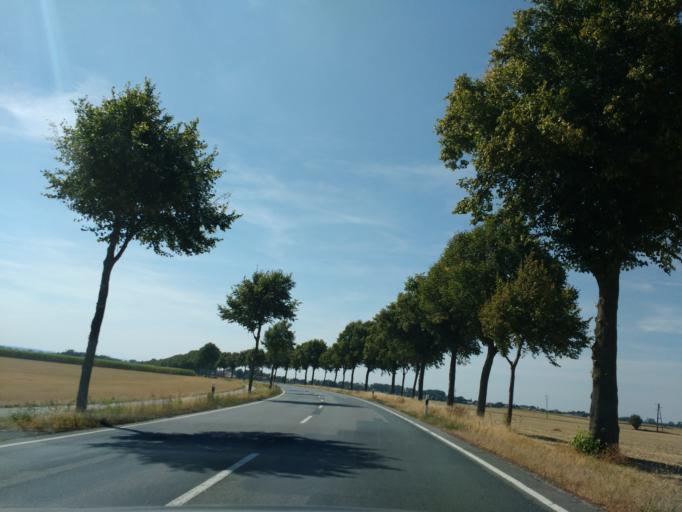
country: DE
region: Lower Saxony
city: Schellerten
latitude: 52.2014
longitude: 10.1394
